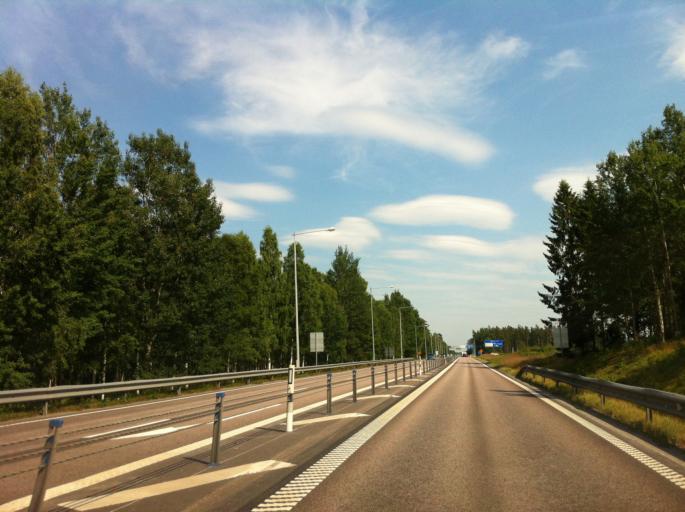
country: SE
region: Kalmar
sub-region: Nybro Kommun
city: Nybro
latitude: 56.7318
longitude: 15.9546
